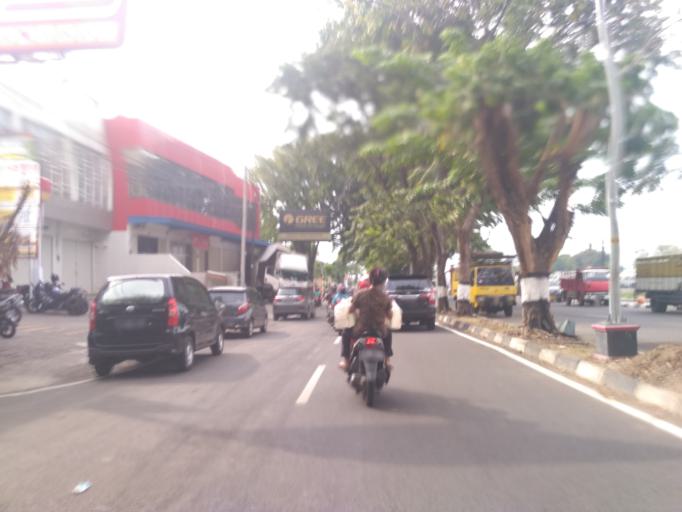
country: ID
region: Central Java
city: Semarang
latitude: -6.9795
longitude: 110.4011
